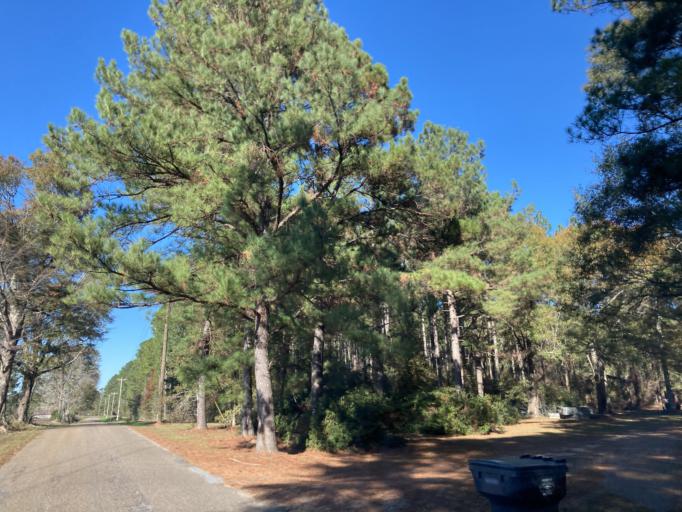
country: US
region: Mississippi
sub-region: Lamar County
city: Sumrall
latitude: 31.3529
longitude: -89.6031
